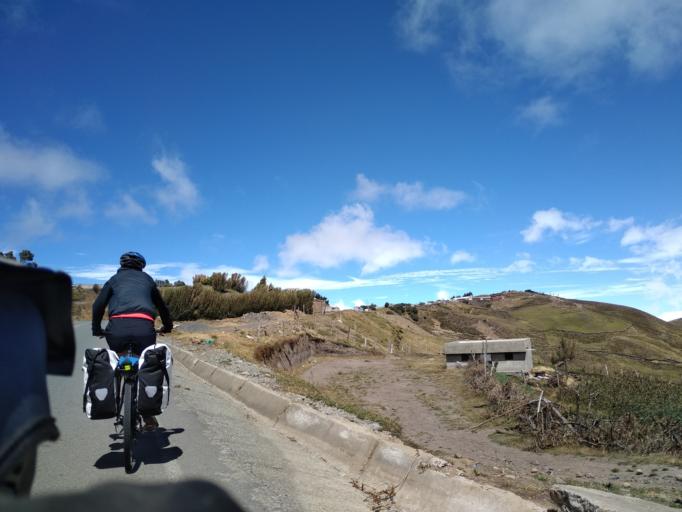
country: EC
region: Cotopaxi
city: Pujili
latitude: -0.9659
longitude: -78.9266
